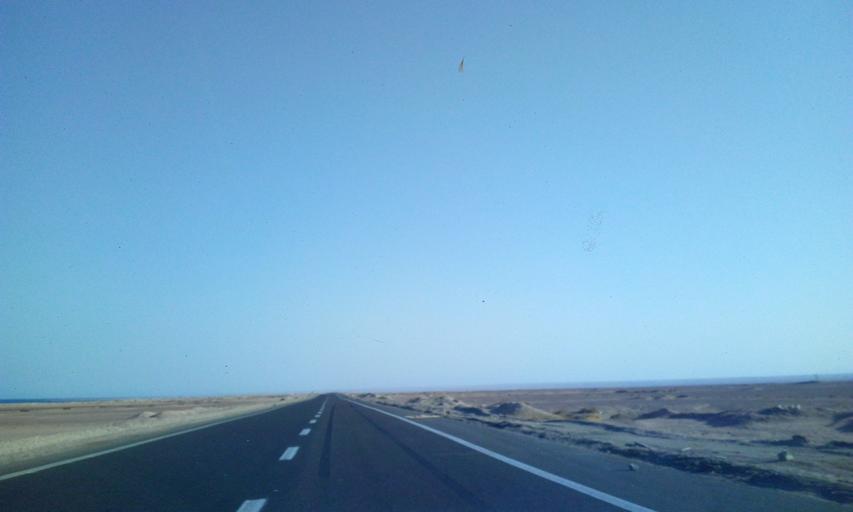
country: EG
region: South Sinai
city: Tor
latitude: 28.6791
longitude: 32.8337
